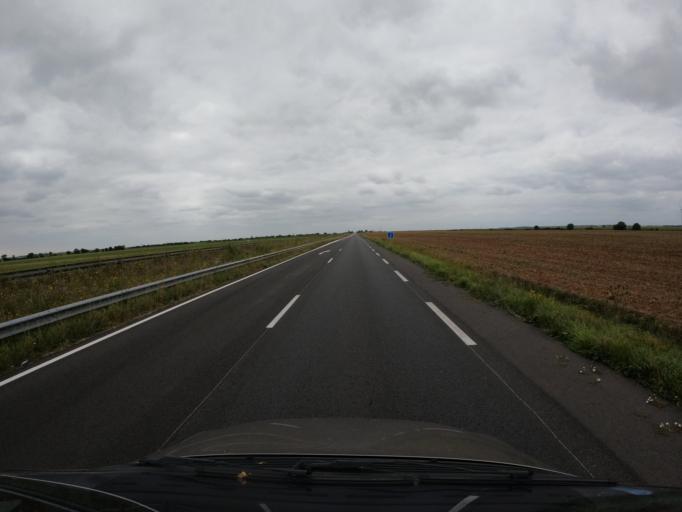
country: FR
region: Pays de la Loire
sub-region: Departement de la Vendee
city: Maillezais
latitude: 46.4266
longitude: -0.7207
